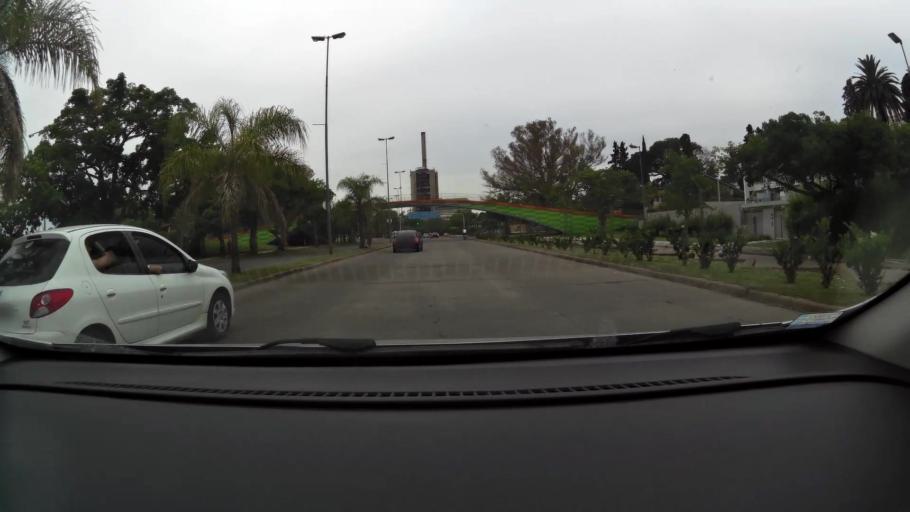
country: AR
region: Santa Fe
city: Granadero Baigorria
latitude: -32.9016
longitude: -60.6822
